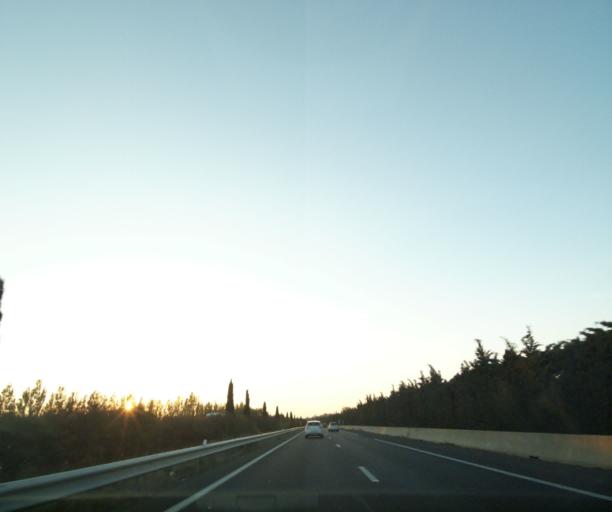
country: FR
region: Provence-Alpes-Cote d'Azur
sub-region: Departement des Bouches-du-Rhone
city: Mouries
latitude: 43.6388
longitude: 4.9115
